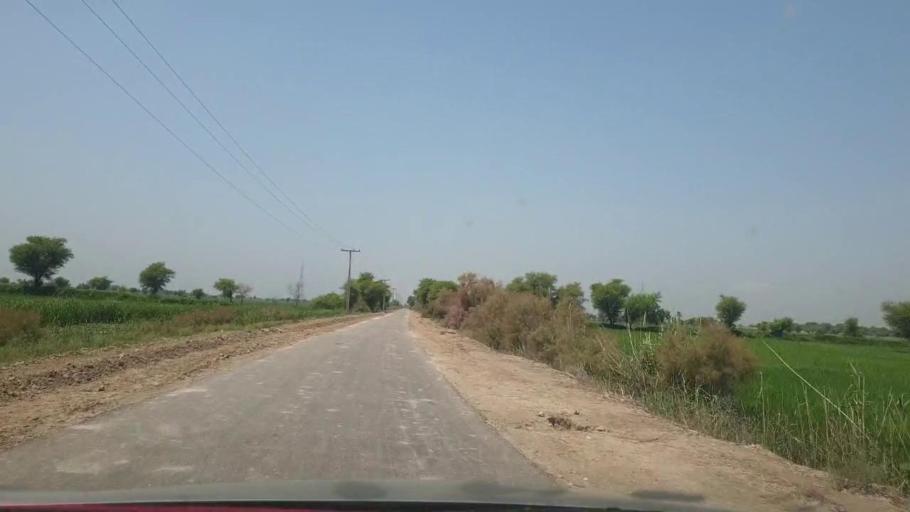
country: PK
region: Sindh
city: Warah
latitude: 27.4830
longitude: 67.7506
